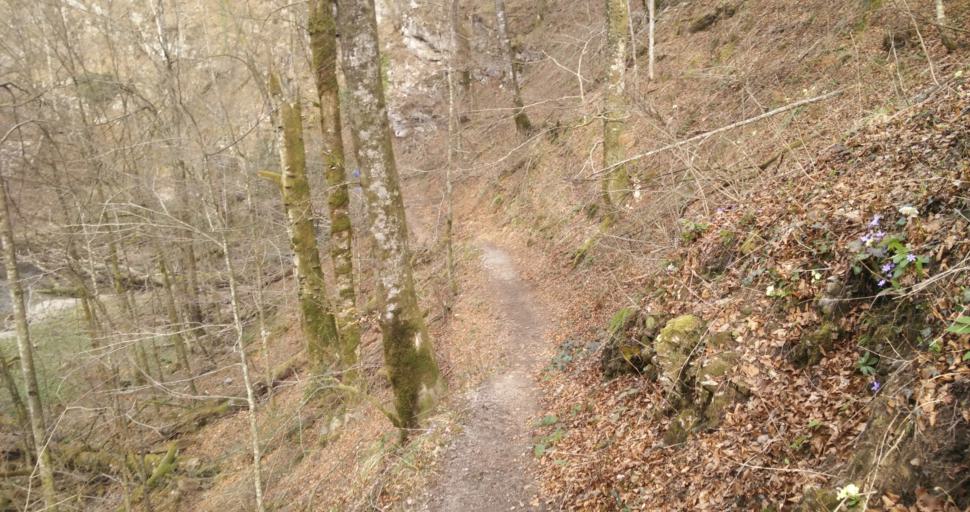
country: HR
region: Primorsko-Goranska
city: Vrbovsko
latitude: 45.3593
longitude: 15.0663
